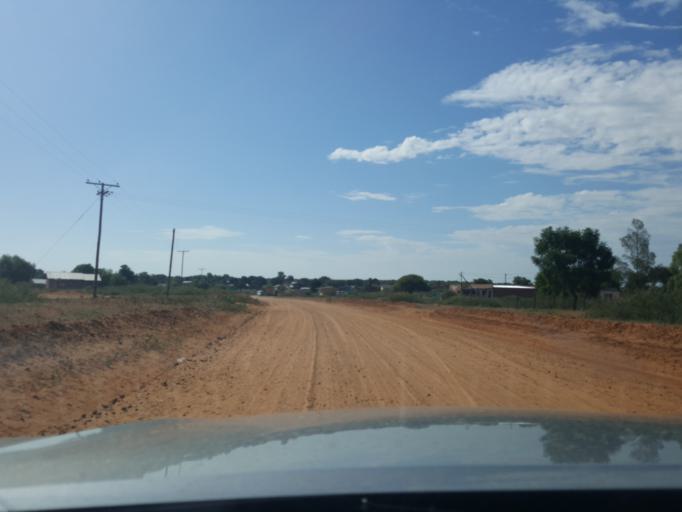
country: BW
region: Kweneng
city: Khudumelapye
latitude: -23.6989
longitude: 24.7200
